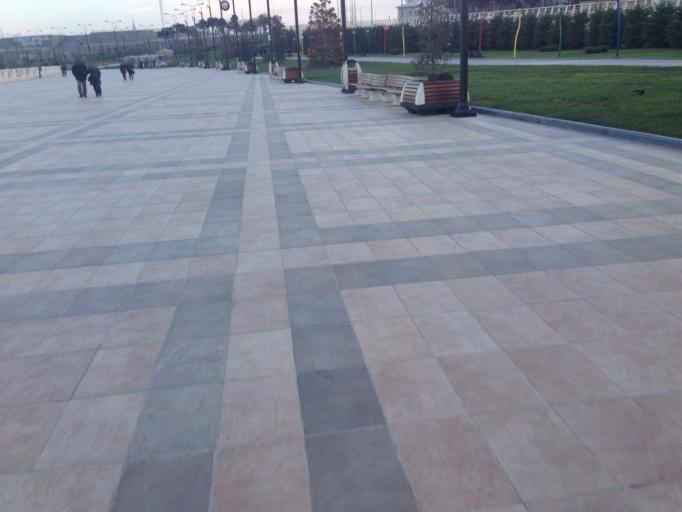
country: AZ
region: Baki
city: Badamdar
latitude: 40.3479
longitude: 49.8392
